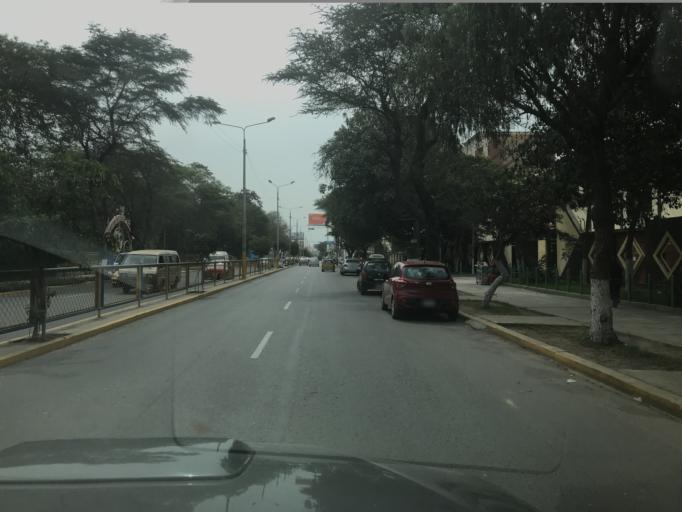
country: PE
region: Lambayeque
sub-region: Provincia de Chiclayo
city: Chiclayo
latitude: -6.7710
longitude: -79.8472
